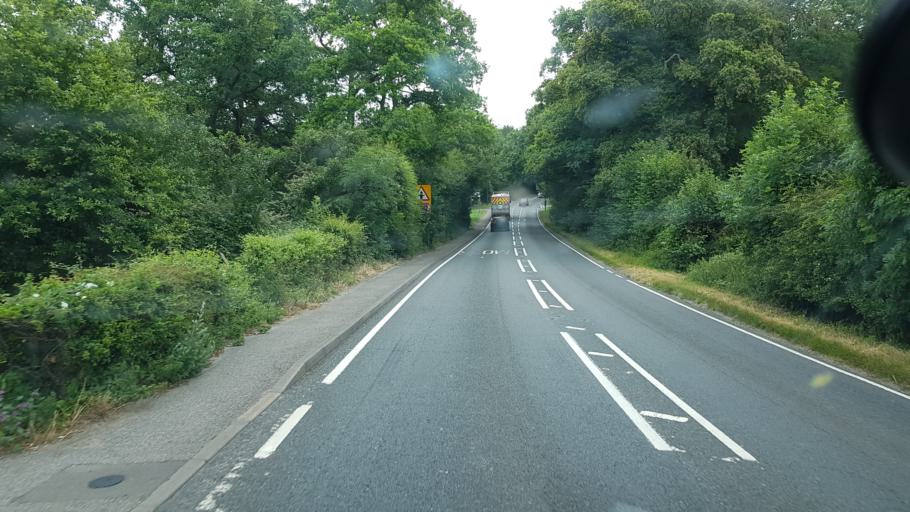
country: GB
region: England
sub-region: Surrey
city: Godstone
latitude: 51.2285
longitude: -0.0474
